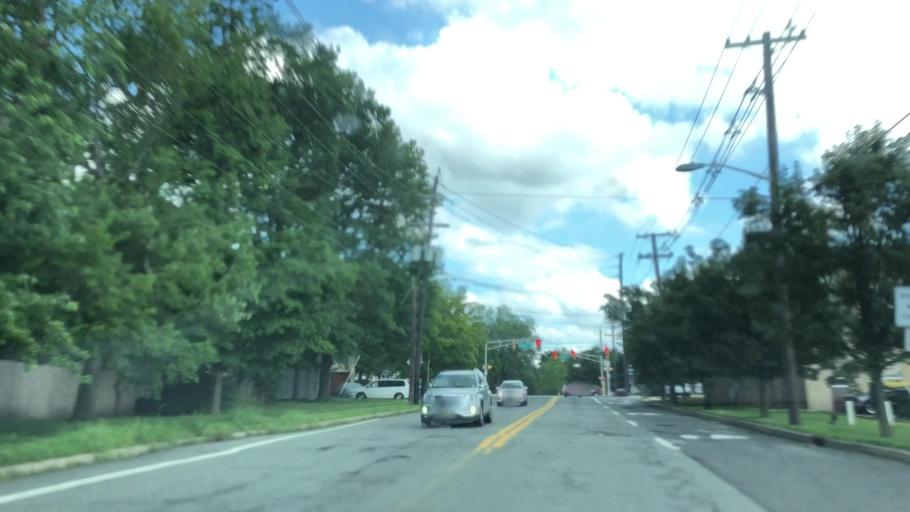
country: US
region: New Jersey
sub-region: Bergen County
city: Rochelle Park
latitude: 40.9114
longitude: -74.0737
